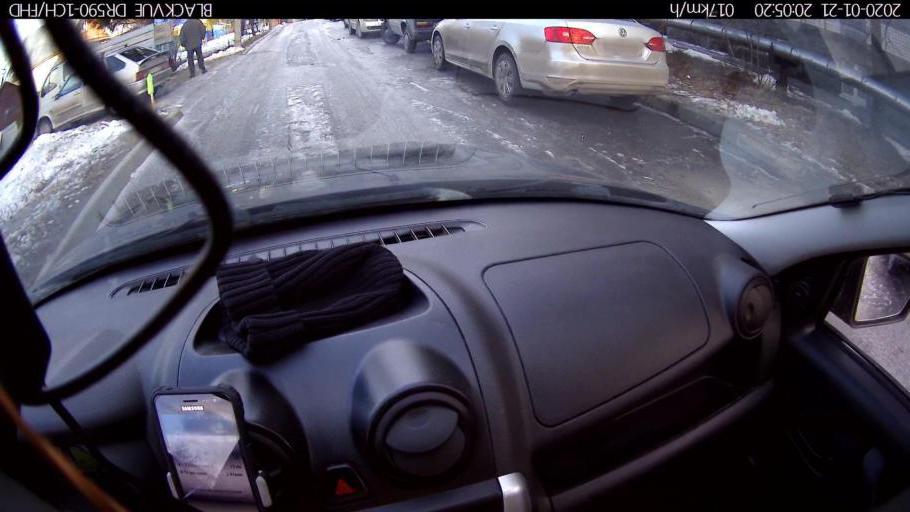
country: RU
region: Nizjnij Novgorod
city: Nizhniy Novgorod
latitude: 56.2922
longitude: 44.0334
